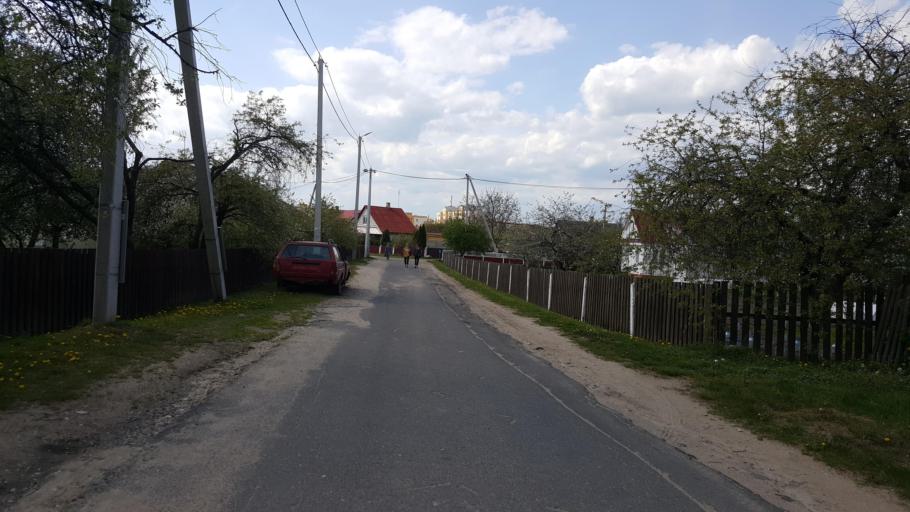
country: BY
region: Brest
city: Kamyanyets
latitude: 52.3930
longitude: 23.8296
